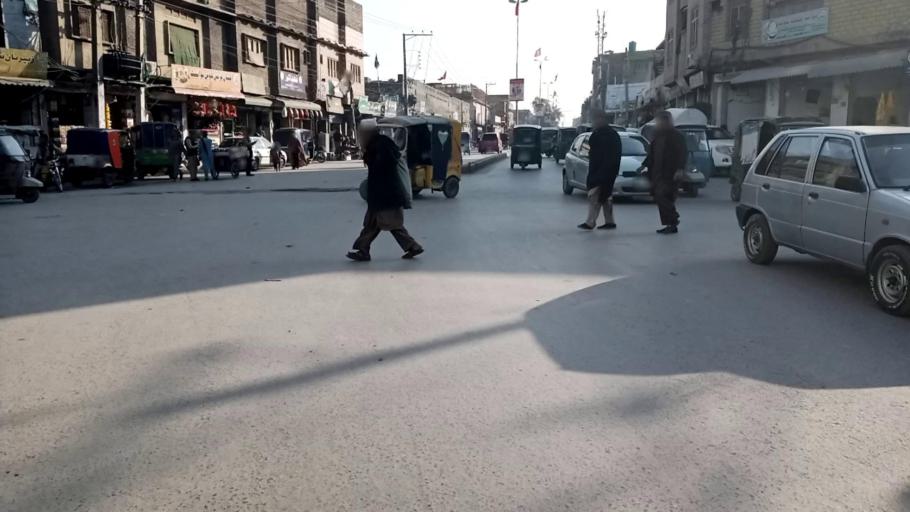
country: PK
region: Khyber Pakhtunkhwa
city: Peshawar
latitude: 34.0138
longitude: 71.5860
